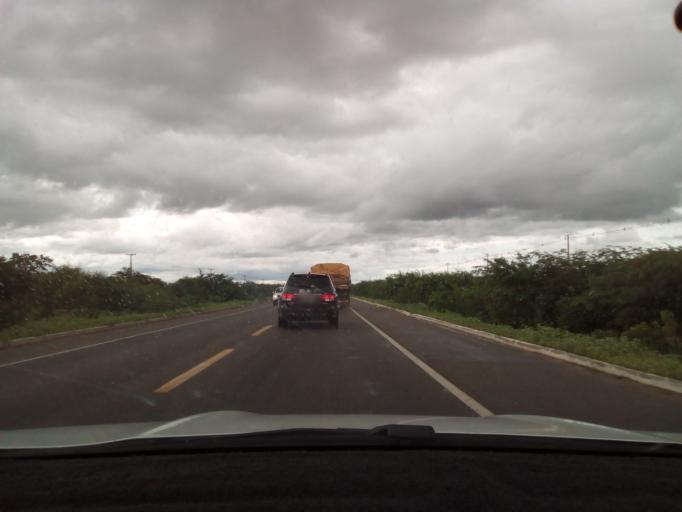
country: BR
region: Rio Grande do Norte
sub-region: Barauna
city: Barauna
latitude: -4.9178
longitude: -37.4231
